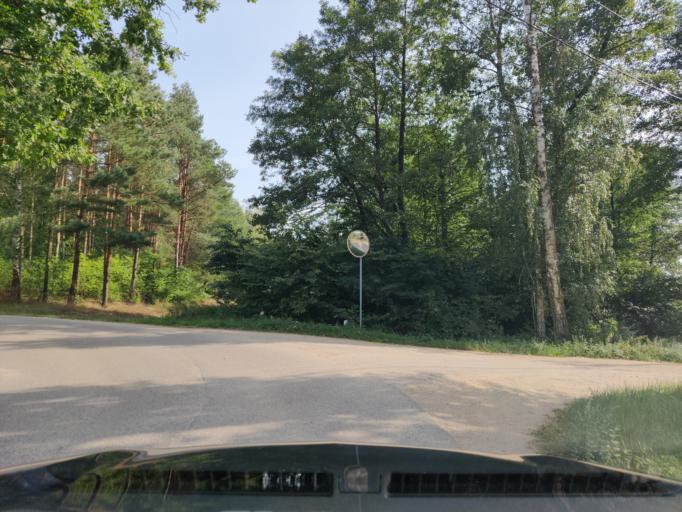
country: PL
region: Masovian Voivodeship
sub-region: Powiat makowski
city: Rozan
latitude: 52.8476
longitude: 21.4581
